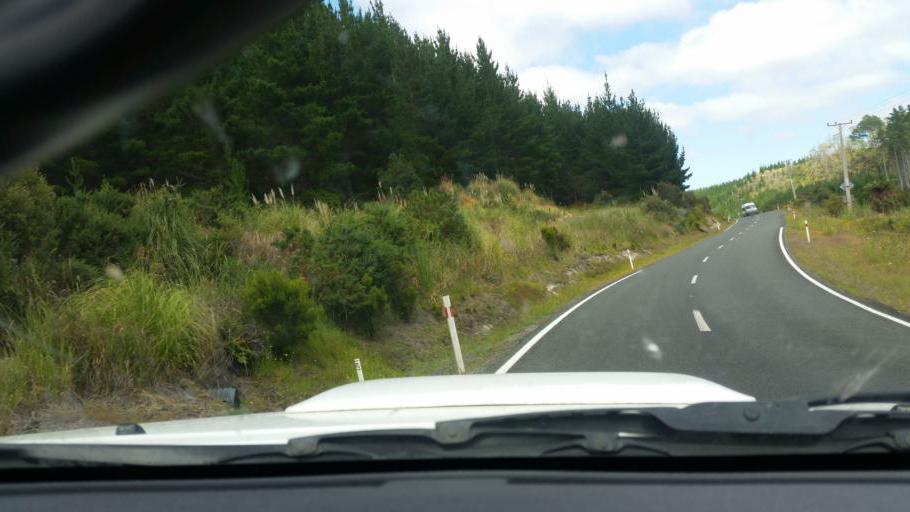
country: NZ
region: Northland
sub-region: Kaipara District
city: Dargaville
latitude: -35.8164
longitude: 173.7175
